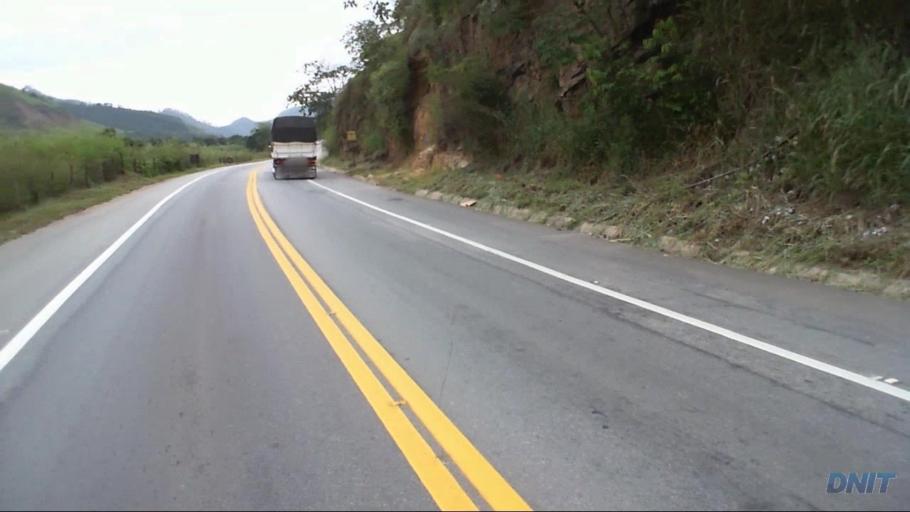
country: BR
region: Minas Gerais
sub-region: Timoteo
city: Timoteo
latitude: -19.6097
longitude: -42.7659
